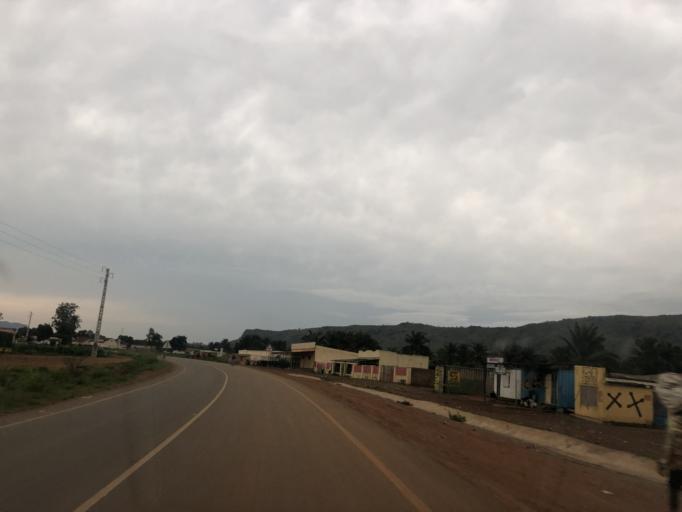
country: AO
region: Cuanza Sul
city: Uacu Cungo
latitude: -11.3482
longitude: 15.1049
